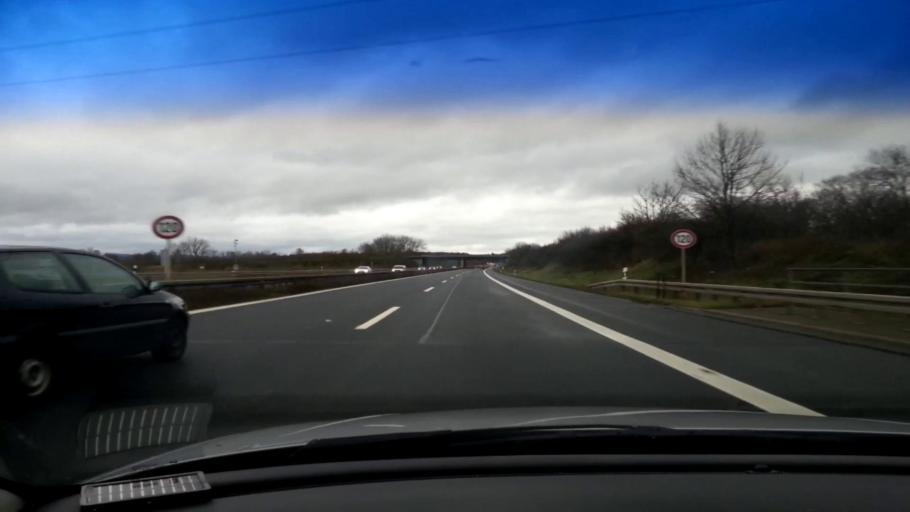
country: DE
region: Bavaria
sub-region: Upper Franconia
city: Gundelsheim
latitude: 49.9340
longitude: 10.9133
